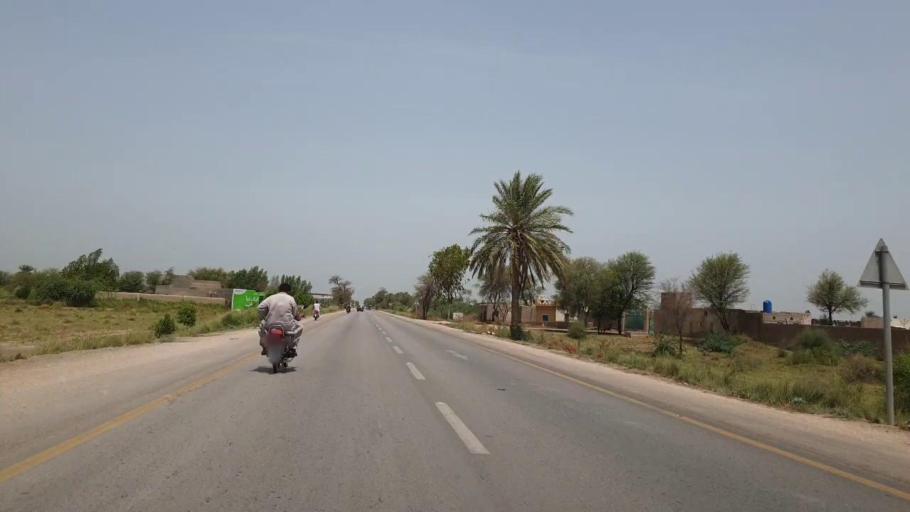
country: PK
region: Sindh
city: Nawabshah
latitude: 26.2156
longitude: 68.5073
